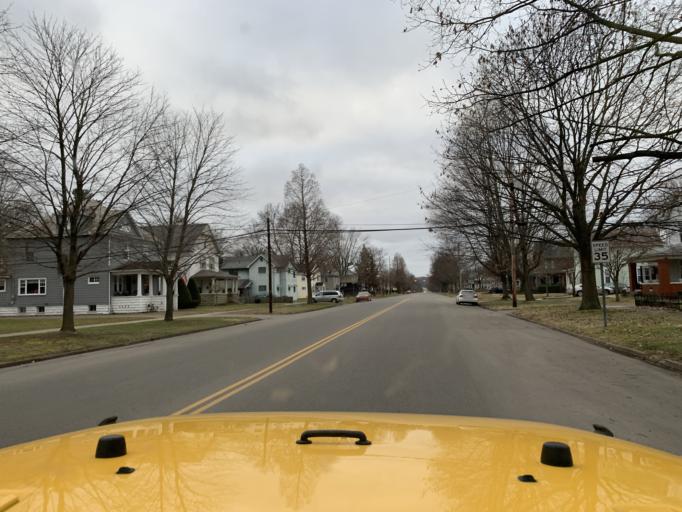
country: US
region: Ohio
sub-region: Tuscarawas County
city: Dover
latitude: 40.5278
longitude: -81.4693
